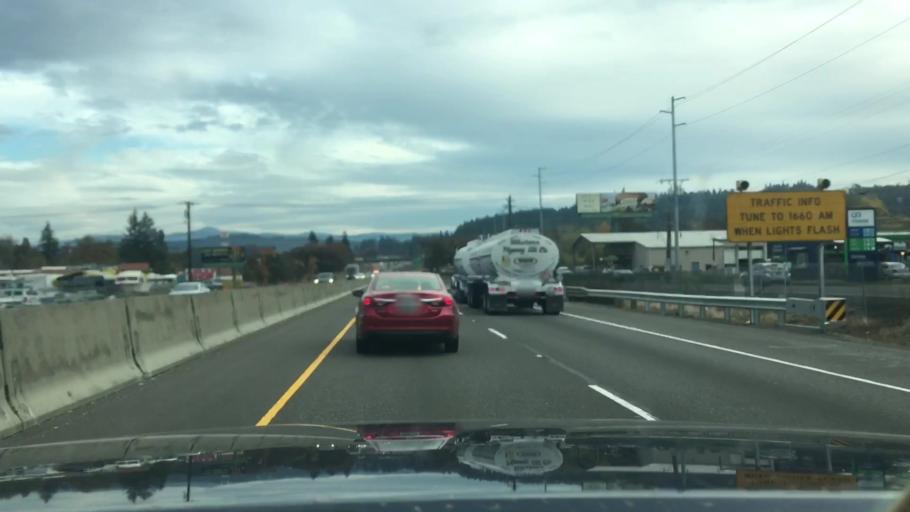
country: US
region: Oregon
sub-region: Lane County
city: Springfield
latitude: 44.0190
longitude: -123.0258
